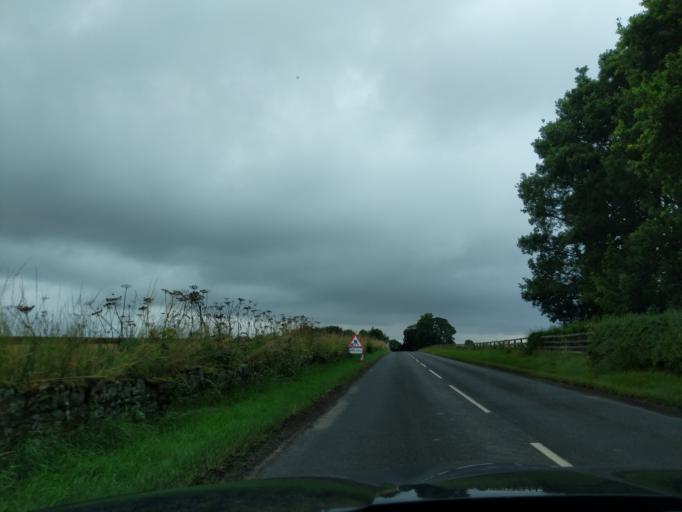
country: GB
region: England
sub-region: Northumberland
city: Ford
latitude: 55.6432
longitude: -2.1090
